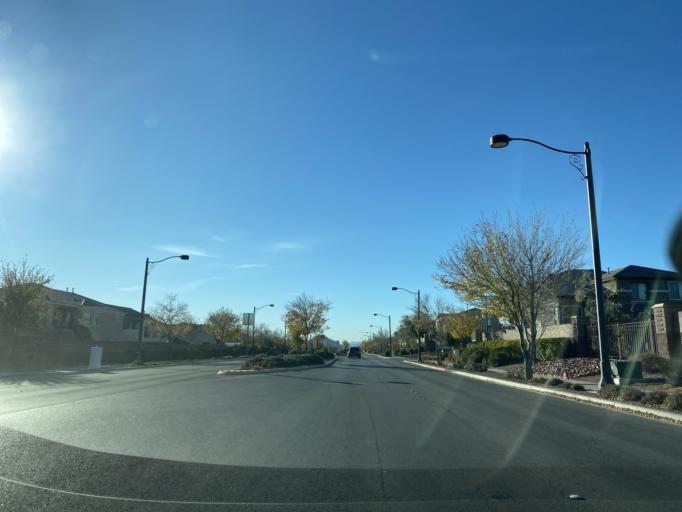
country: US
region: Nevada
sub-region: Clark County
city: Summerlin South
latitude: 36.2947
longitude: -115.3196
